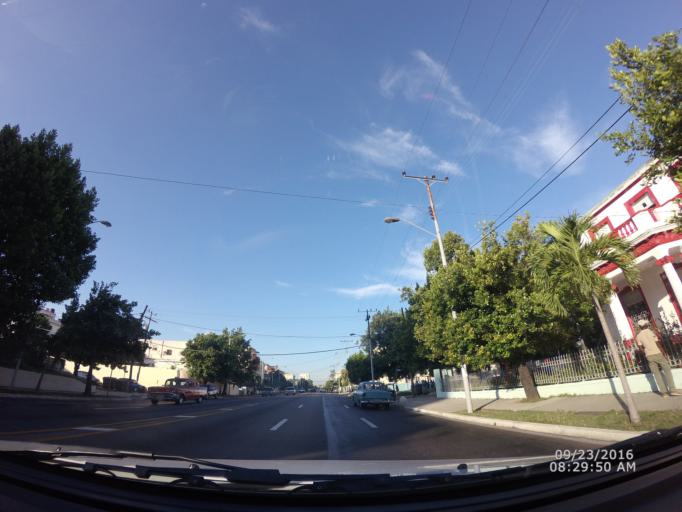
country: CU
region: La Habana
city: Havana
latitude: 23.1306
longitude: -82.3951
